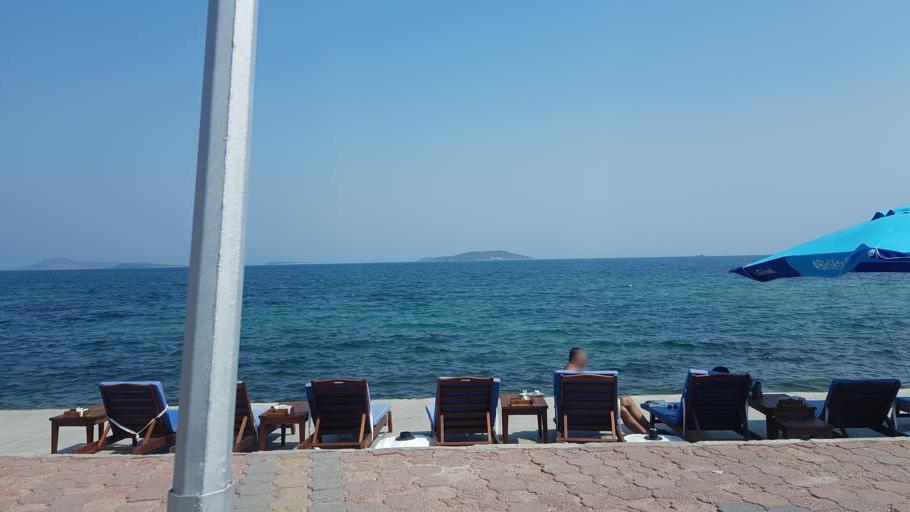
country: TR
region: Izmir
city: Urla
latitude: 38.3665
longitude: 26.7665
